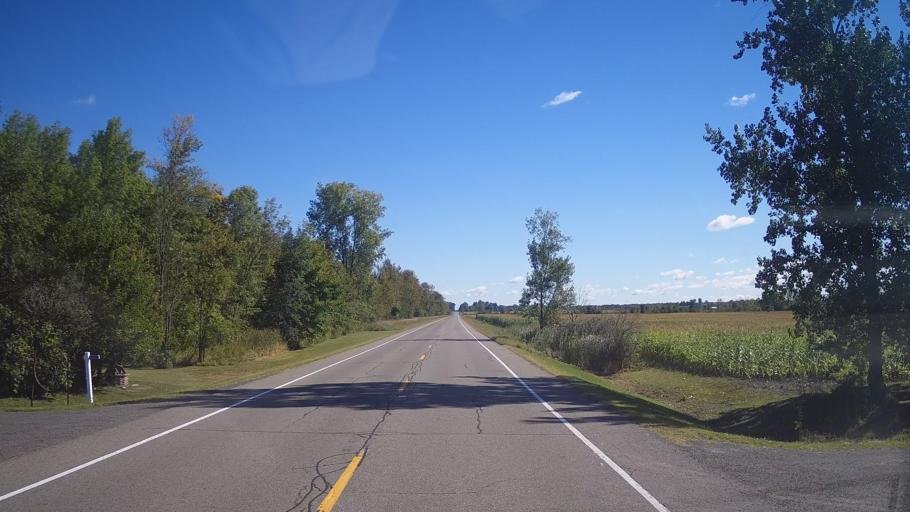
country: CA
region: Ontario
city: Prescott
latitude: 44.9308
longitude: -75.3306
